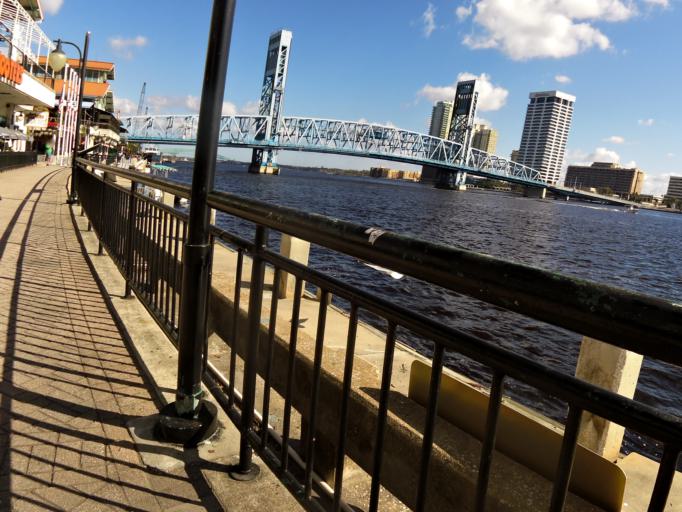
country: US
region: Florida
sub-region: Duval County
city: Jacksonville
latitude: 30.3245
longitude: -81.6606
